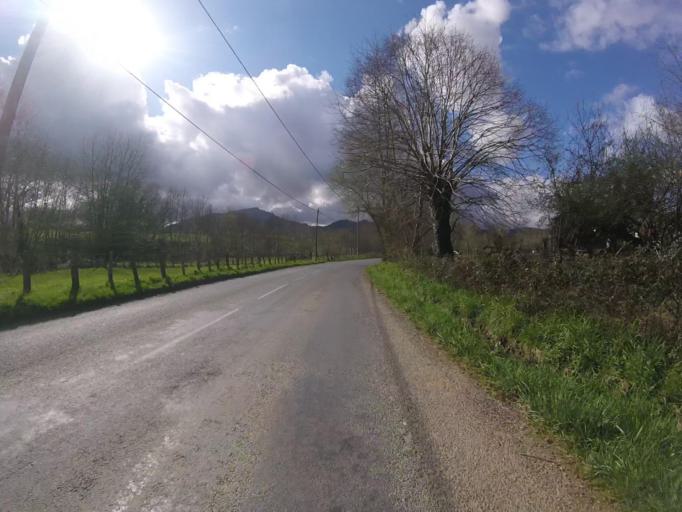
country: FR
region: Aquitaine
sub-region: Departement des Pyrenees-Atlantiques
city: Sare
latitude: 43.2908
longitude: -1.5792
